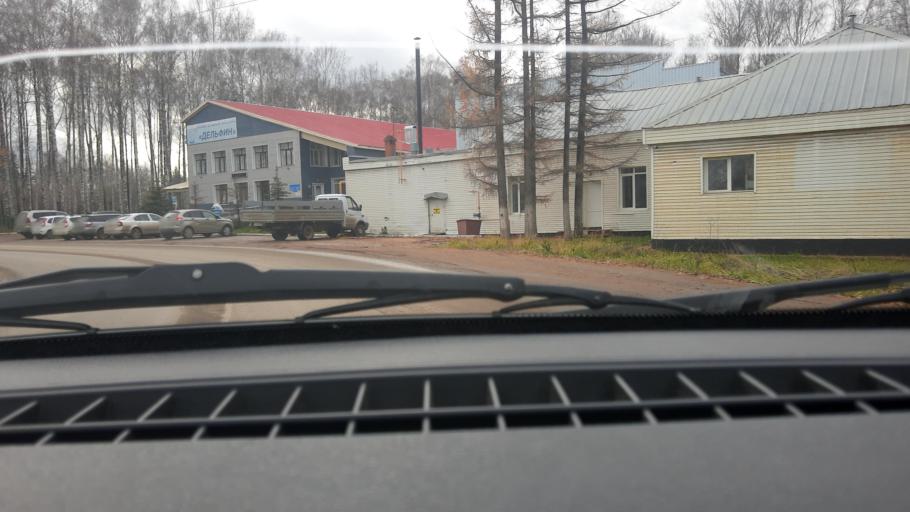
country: RU
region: Bashkortostan
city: Iglino
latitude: 54.8334
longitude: 56.4224
